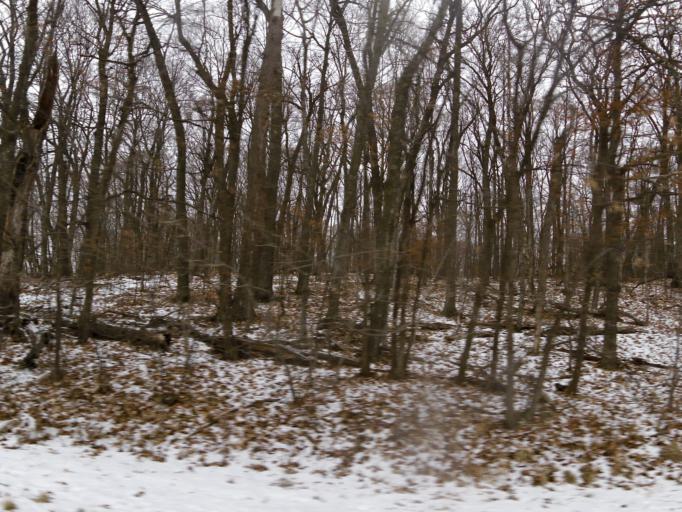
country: US
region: Minnesota
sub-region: Hennepin County
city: Medina
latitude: 45.0255
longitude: -93.5876
